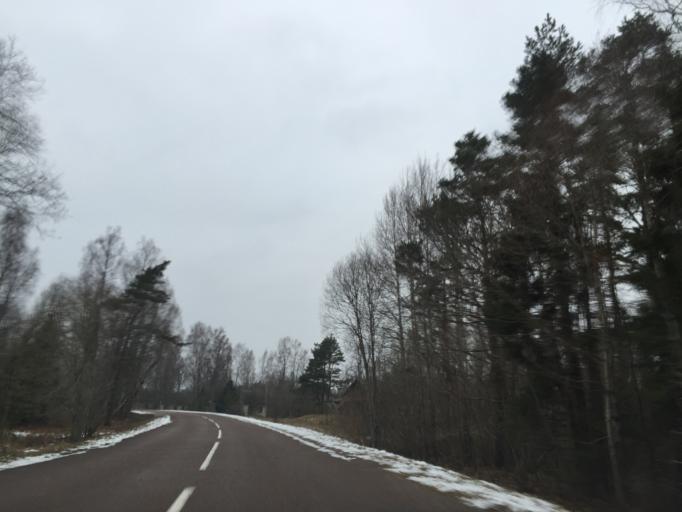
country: EE
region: Saare
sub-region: Kuressaare linn
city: Kuressaare
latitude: 58.3921
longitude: 22.2088
